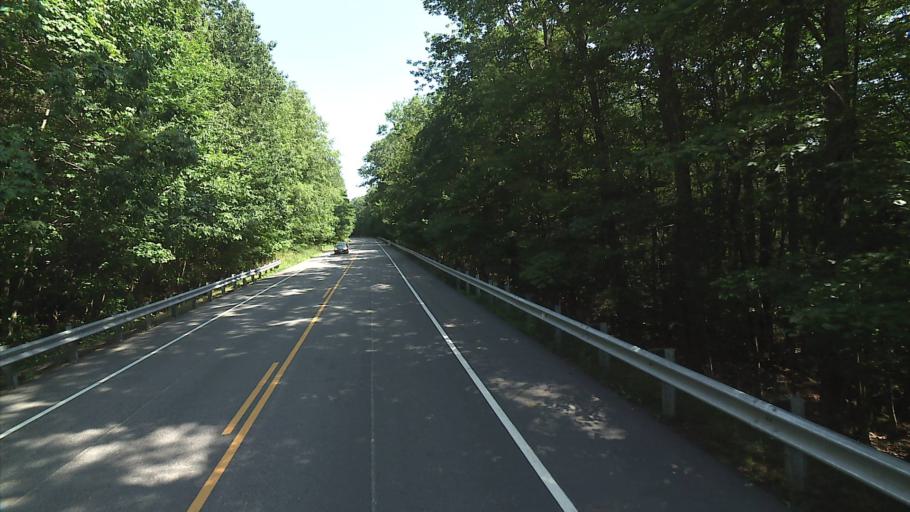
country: US
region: Connecticut
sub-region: Litchfield County
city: Winchester Center
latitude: 41.8750
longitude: -73.1694
